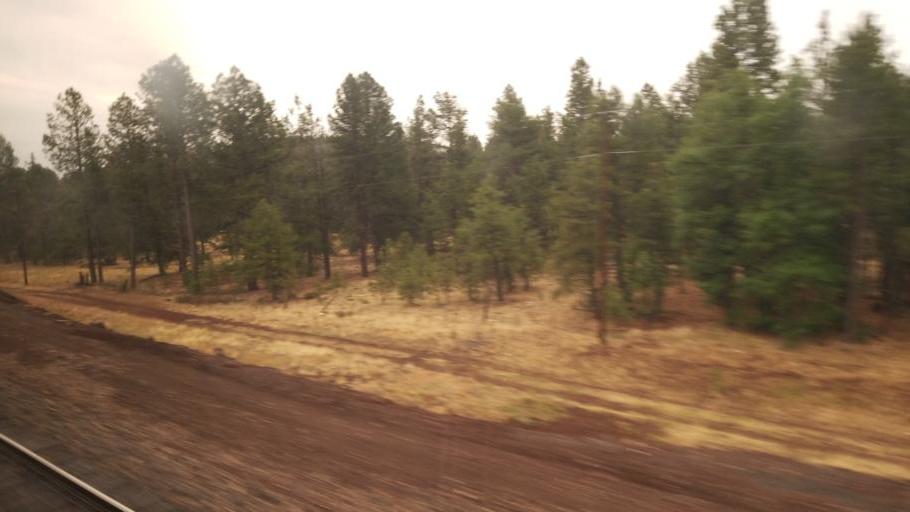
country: US
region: Arizona
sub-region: Coconino County
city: Parks
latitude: 35.2533
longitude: -111.9358
